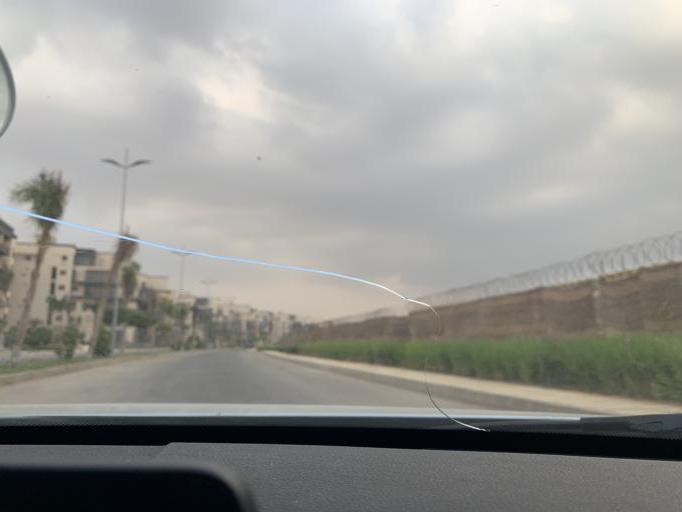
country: EG
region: Muhafazat al Qalyubiyah
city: Al Khankah
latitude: 30.0988
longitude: 31.6591
